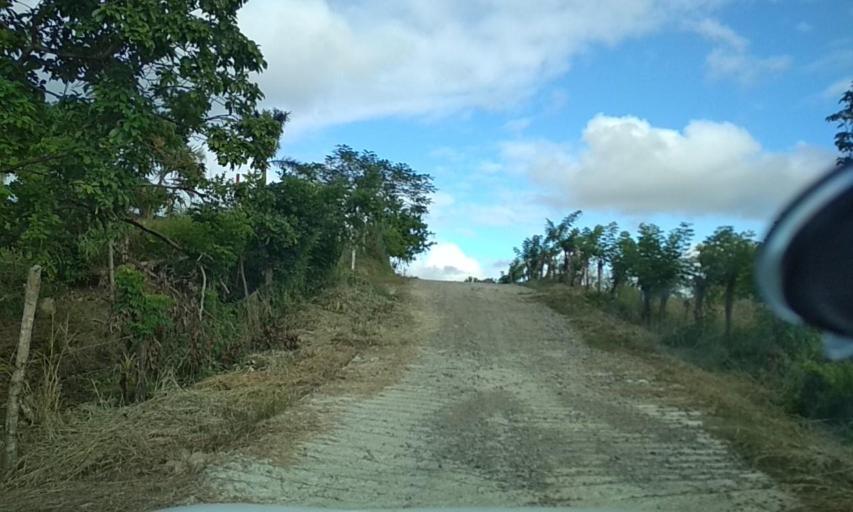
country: MX
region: Veracruz
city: Cazones de Herrera
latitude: 20.6478
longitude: -97.3409
